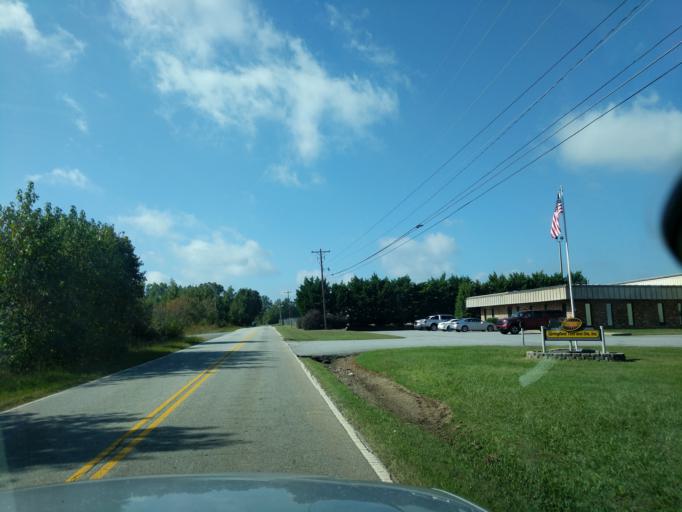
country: US
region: South Carolina
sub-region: Spartanburg County
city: Duncan
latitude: 34.8895
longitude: -82.1454
